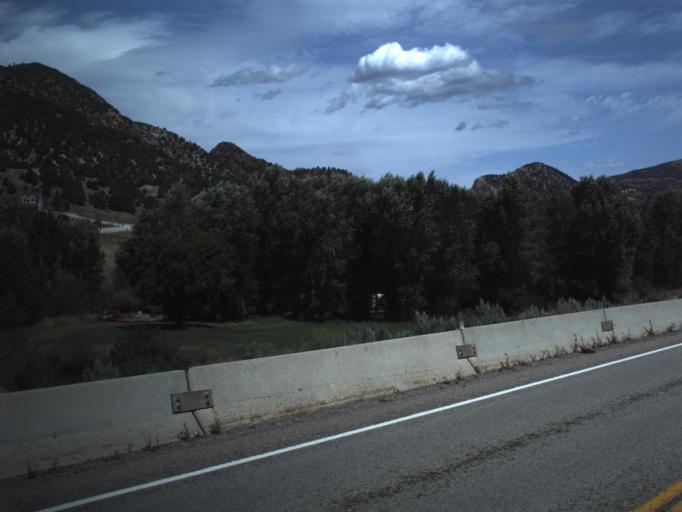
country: US
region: Utah
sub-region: Utah County
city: Woodland Hills
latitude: 39.9728
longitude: -111.5066
